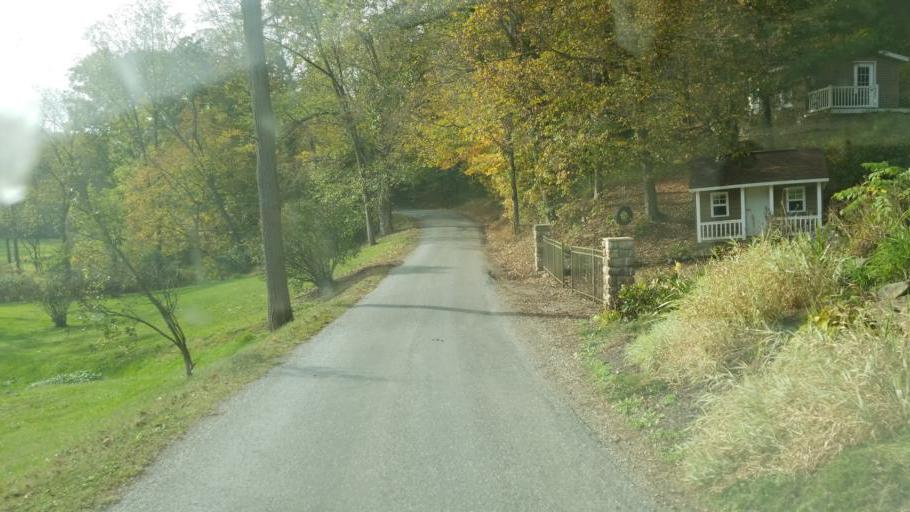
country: US
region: Ohio
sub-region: Holmes County
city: Millersburg
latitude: 40.5329
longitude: -81.8594
